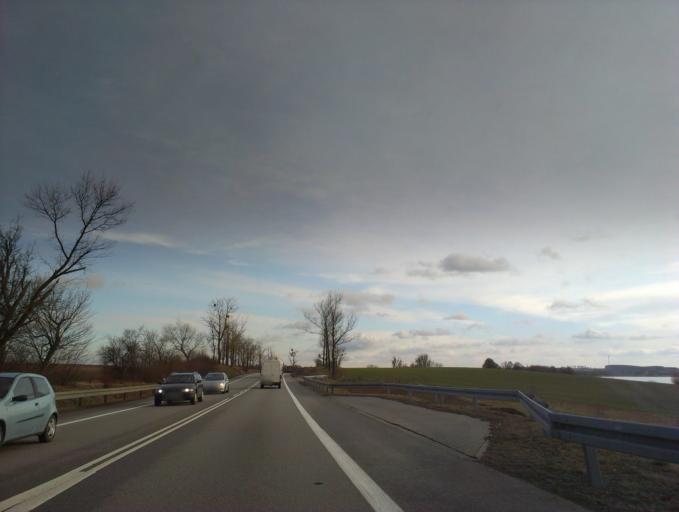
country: PL
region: Kujawsko-Pomorskie
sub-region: Powiat lipnowski
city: Kikol
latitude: 52.9234
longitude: 19.0913
